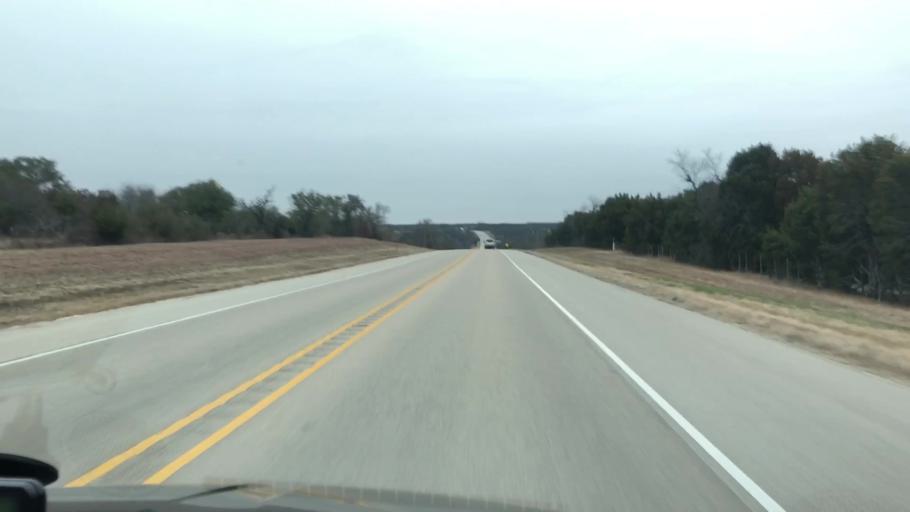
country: US
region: Texas
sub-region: Hamilton County
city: Hamilton
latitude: 31.5767
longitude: -98.1576
